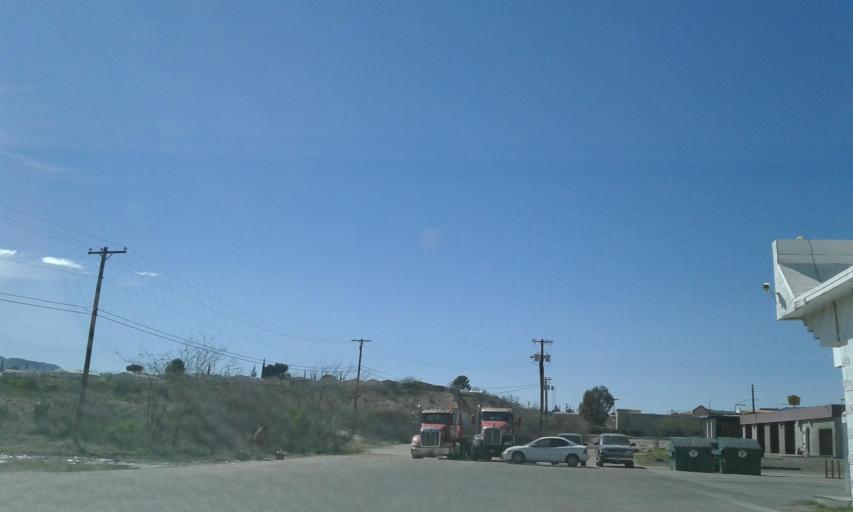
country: US
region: Arizona
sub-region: Gila County
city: Central Heights-Midland City
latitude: 33.4187
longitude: -110.8127
